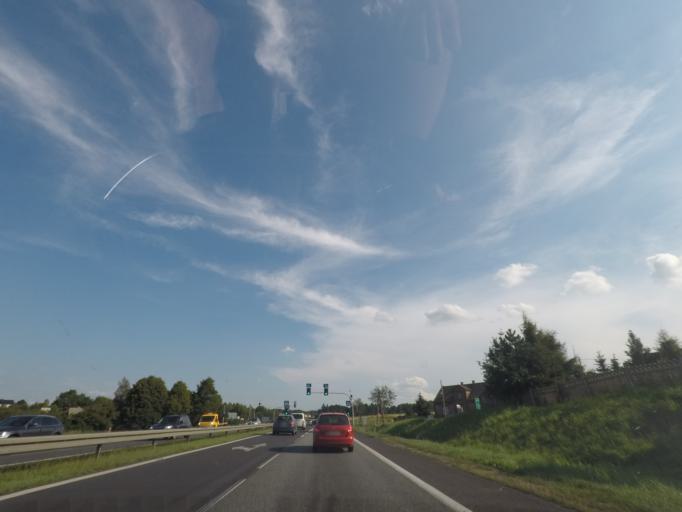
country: PL
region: Silesian Voivodeship
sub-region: Powiat myszkowski
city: Kozieglowy
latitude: 50.5718
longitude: 19.1653
